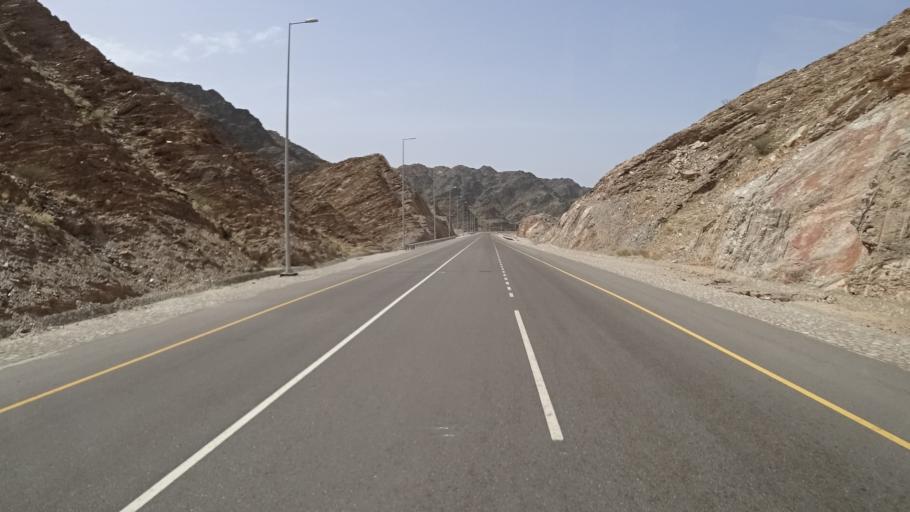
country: OM
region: Muhafazat Masqat
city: Muscat
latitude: 23.4465
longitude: 58.7574
